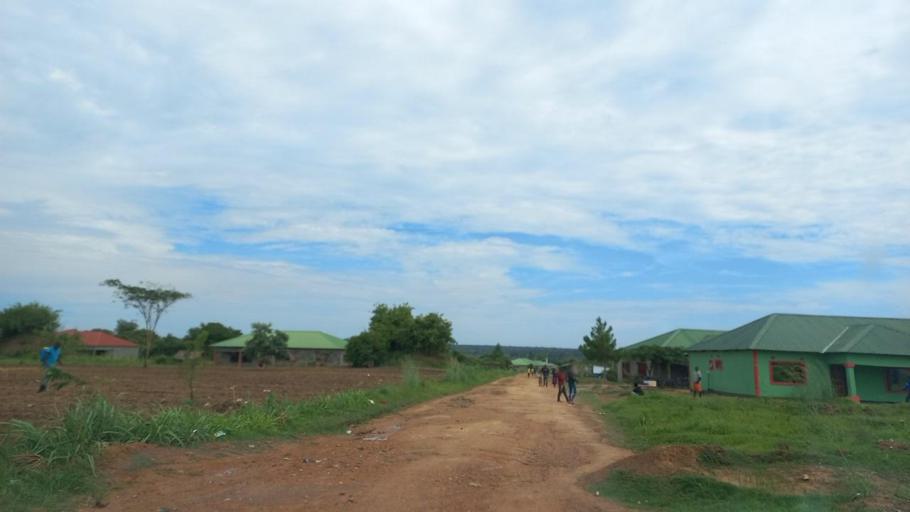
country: ZM
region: Copperbelt
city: Kitwe
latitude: -12.8720
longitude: 28.3340
